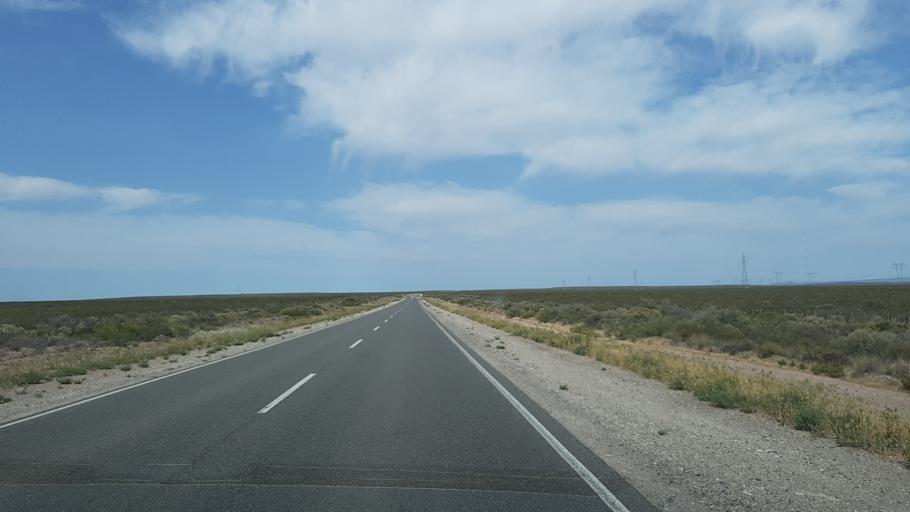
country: AR
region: Neuquen
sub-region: Departamento de Picun Leufu
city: Picun Leufu
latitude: -39.7399
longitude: -69.5996
